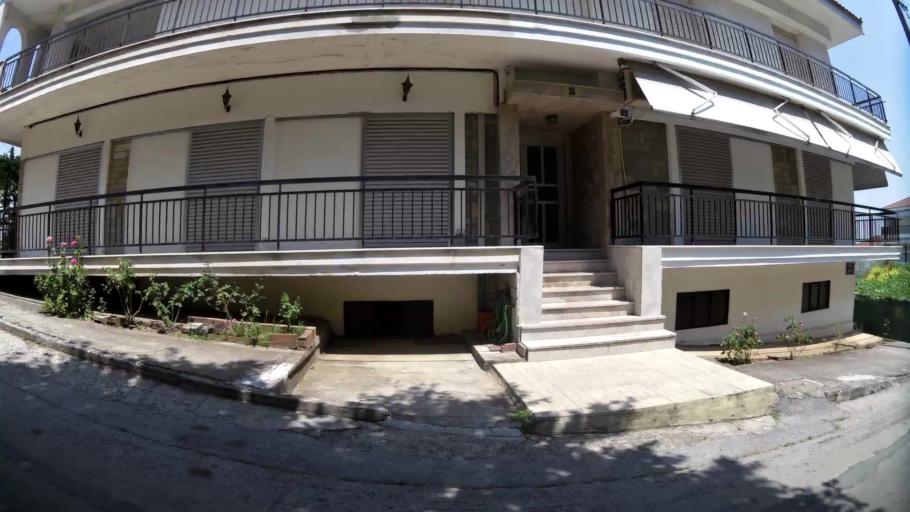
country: GR
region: Central Macedonia
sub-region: Nomos Imathias
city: Veroia
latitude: 40.5105
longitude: 22.2077
